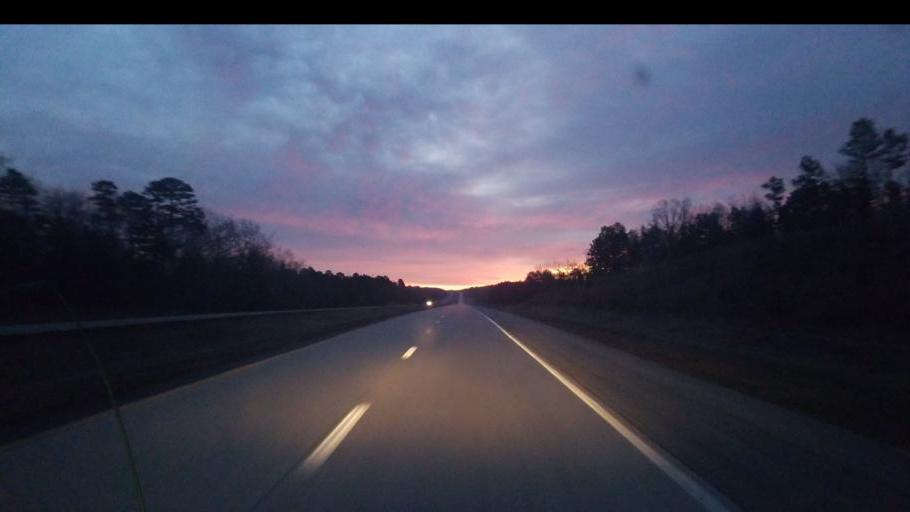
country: US
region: Missouri
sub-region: Shannon County
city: Winona
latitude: 36.9981
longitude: -91.4026
